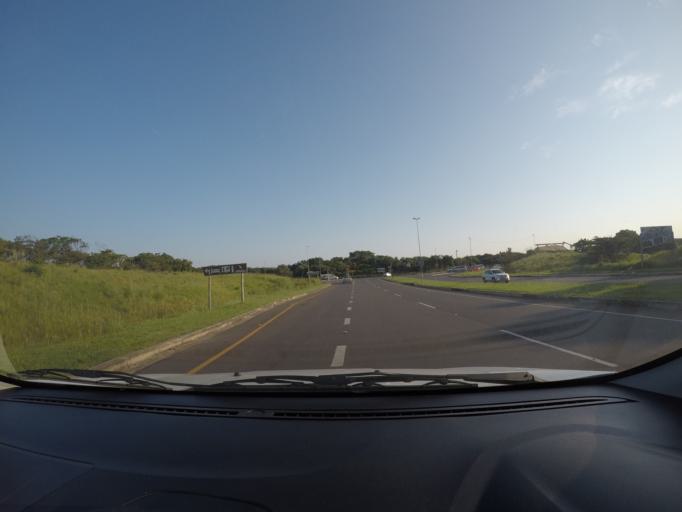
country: ZA
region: KwaZulu-Natal
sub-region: uThungulu District Municipality
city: Richards Bay
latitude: -28.7672
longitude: 32.0485
